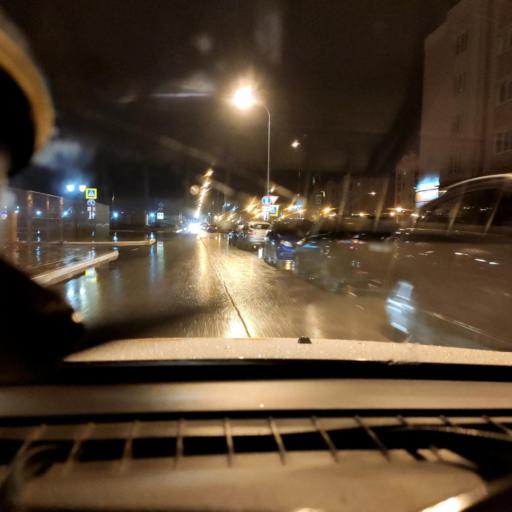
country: RU
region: Samara
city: Samara
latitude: 53.1180
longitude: 50.1636
